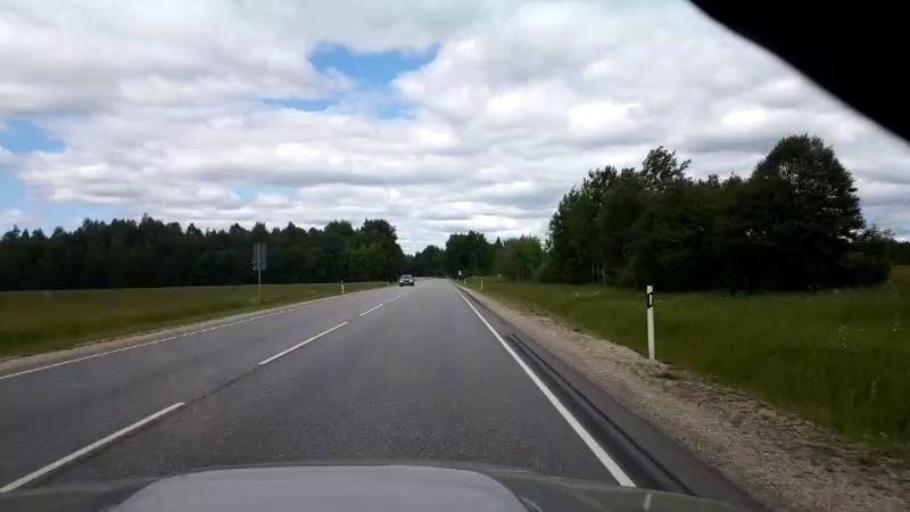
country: EE
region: Raplamaa
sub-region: Maerjamaa vald
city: Marjamaa
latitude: 58.9443
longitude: 24.4675
